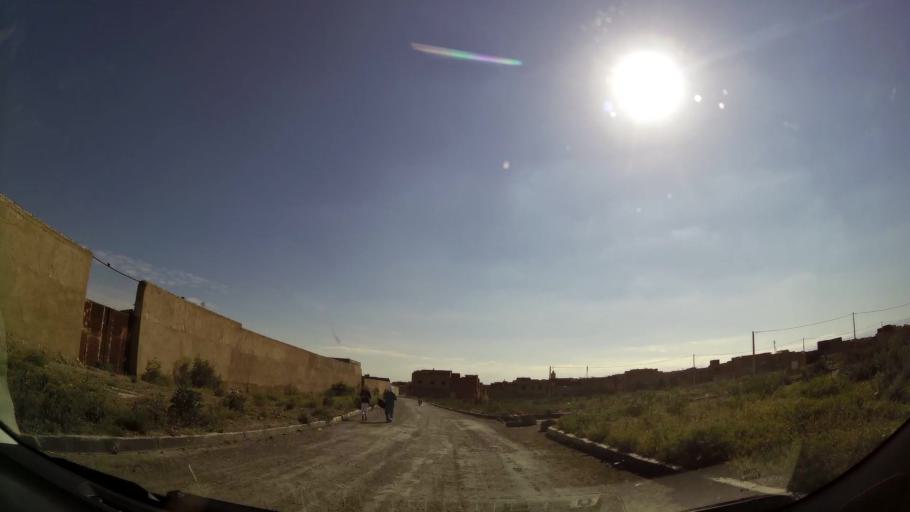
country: MA
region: Oriental
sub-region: Oujda-Angad
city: Oujda
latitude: 34.6558
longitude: -1.9535
